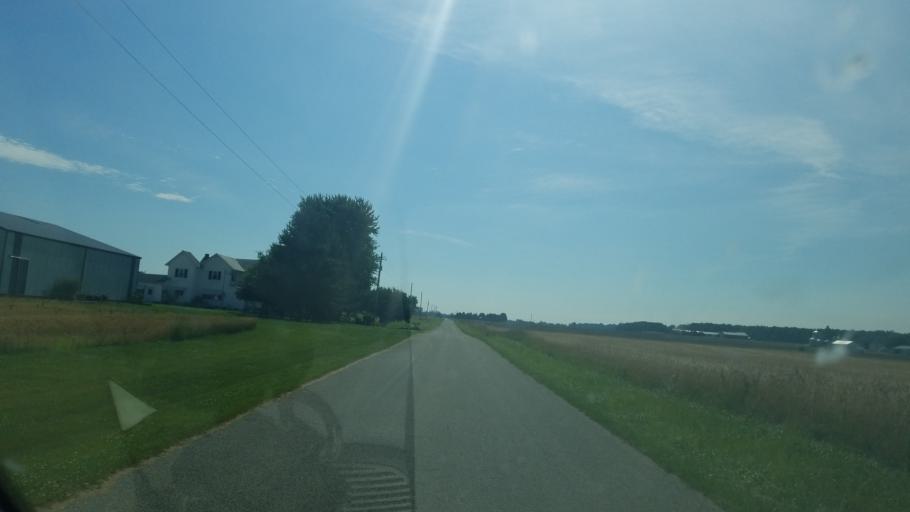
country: US
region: Ohio
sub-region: Wyandot County
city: Carey
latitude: 41.0142
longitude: -83.3471
